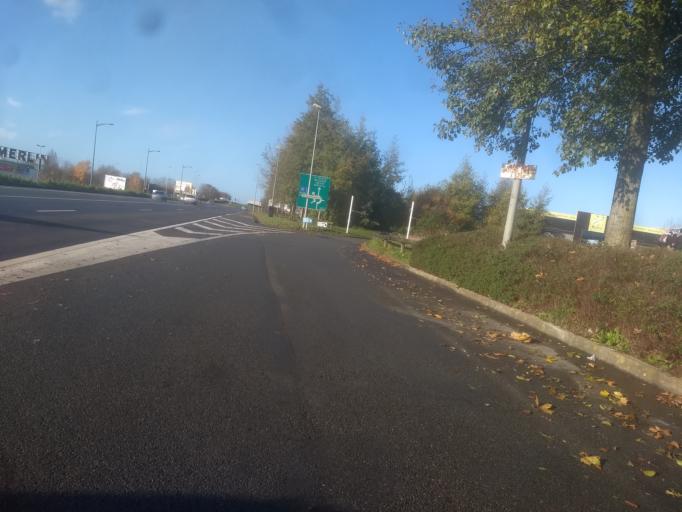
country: FR
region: Nord-Pas-de-Calais
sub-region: Departement du Pas-de-Calais
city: Anzin-Saint-Aubin
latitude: 50.3020
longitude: 2.7304
